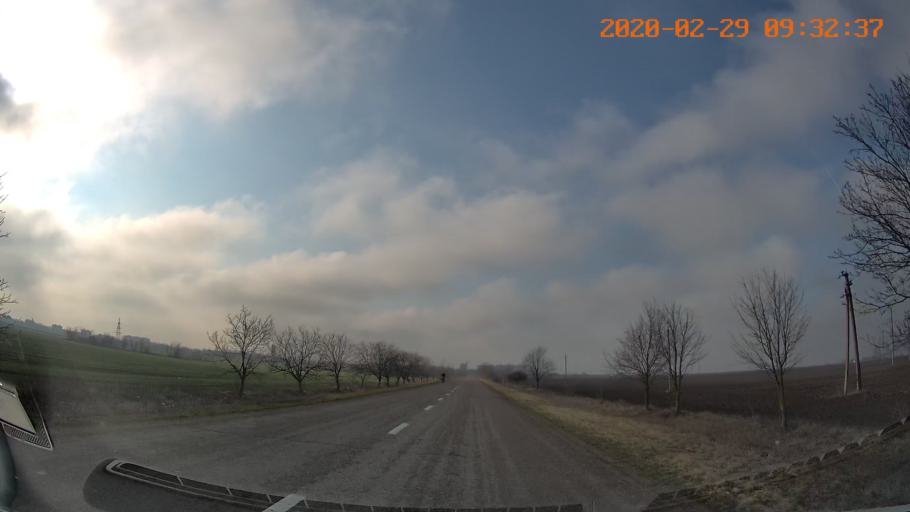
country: MD
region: Telenesti
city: Dnestrovsc
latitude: 46.6371
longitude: 29.9051
